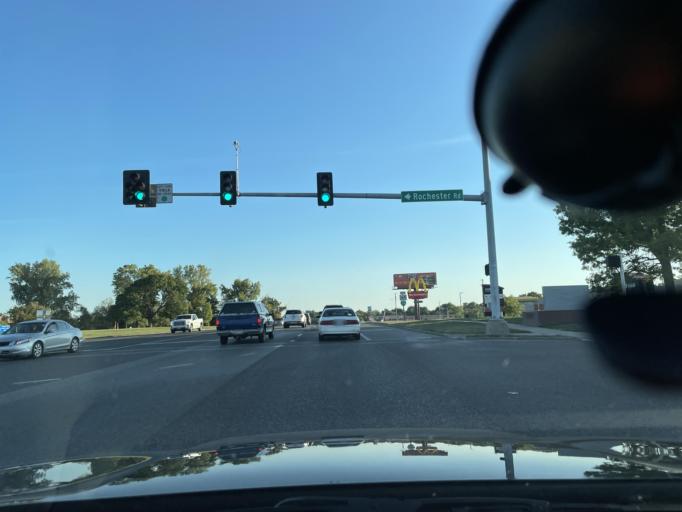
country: US
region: Missouri
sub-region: Andrew County
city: Country Club Village
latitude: 39.8032
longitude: -94.8153
